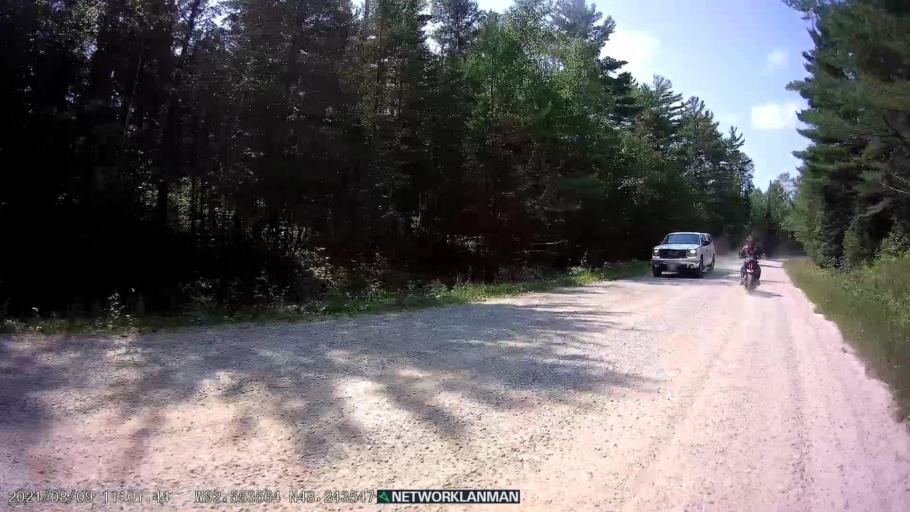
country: US
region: Minnesota
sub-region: Saint Louis County
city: Parkville
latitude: 48.2433
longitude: -92.5535
